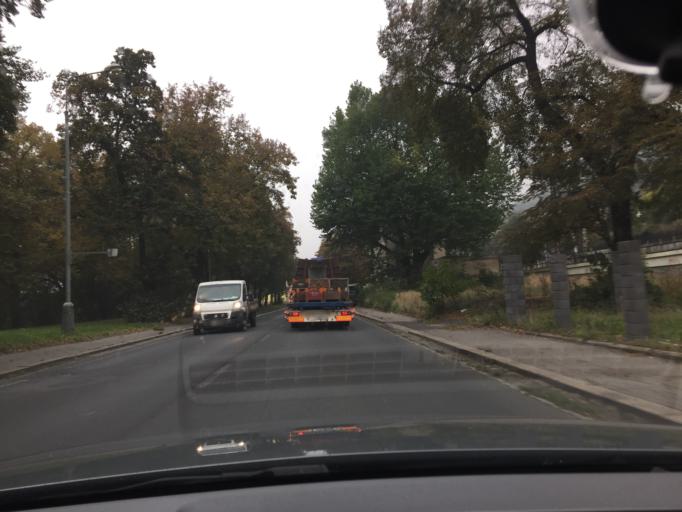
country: CZ
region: Ustecky
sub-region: Okres Usti nad Labem
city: Usti nad Labem
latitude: 50.6522
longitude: 14.0412
